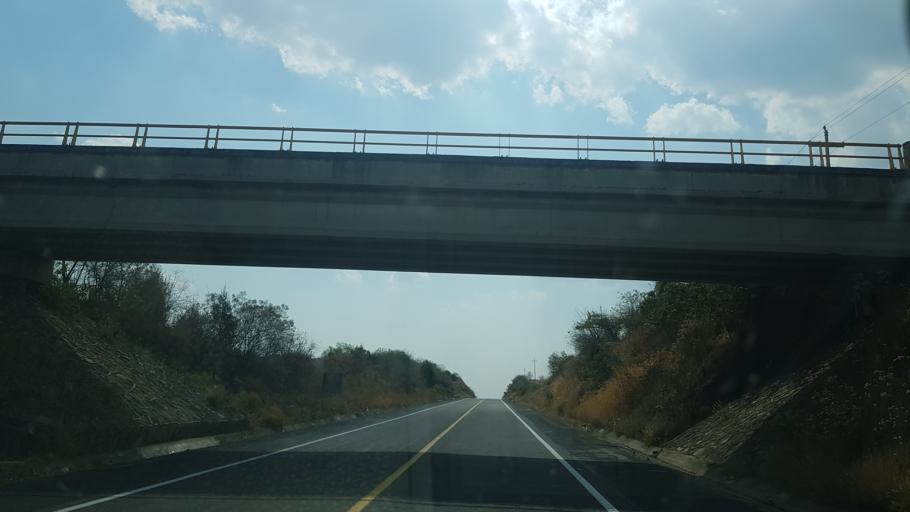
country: MX
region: Puebla
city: San Juan Amecac
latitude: 18.8164
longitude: -98.6630
